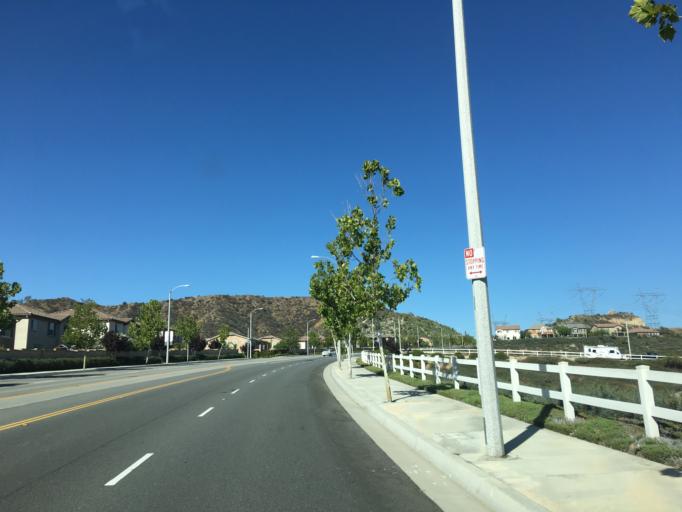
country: US
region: California
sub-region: Los Angeles County
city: Santa Clarita
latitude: 34.4434
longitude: -118.4857
